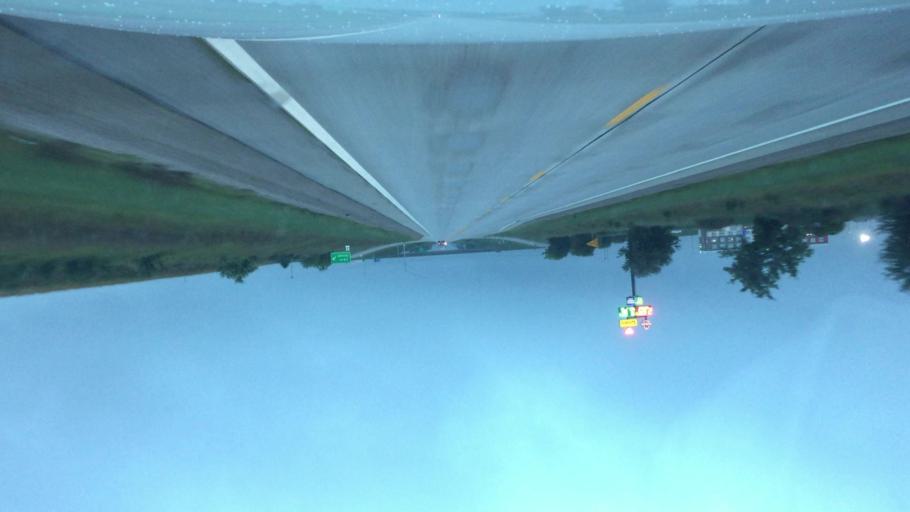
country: US
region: Kansas
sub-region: Neosho County
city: Chanute
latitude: 37.6508
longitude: -95.4797
